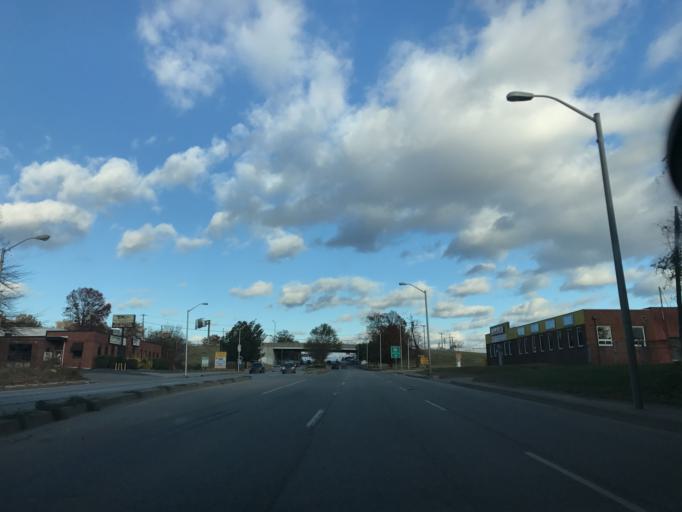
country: US
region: Maryland
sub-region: Baltimore County
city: Rosedale
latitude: 39.3001
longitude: -76.5534
